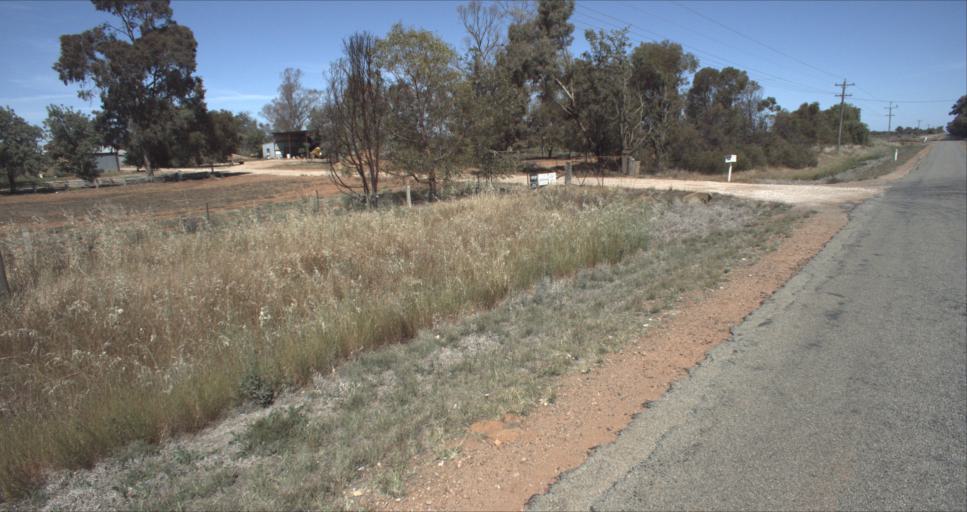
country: AU
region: New South Wales
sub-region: Leeton
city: Leeton
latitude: -34.5802
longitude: 146.2825
